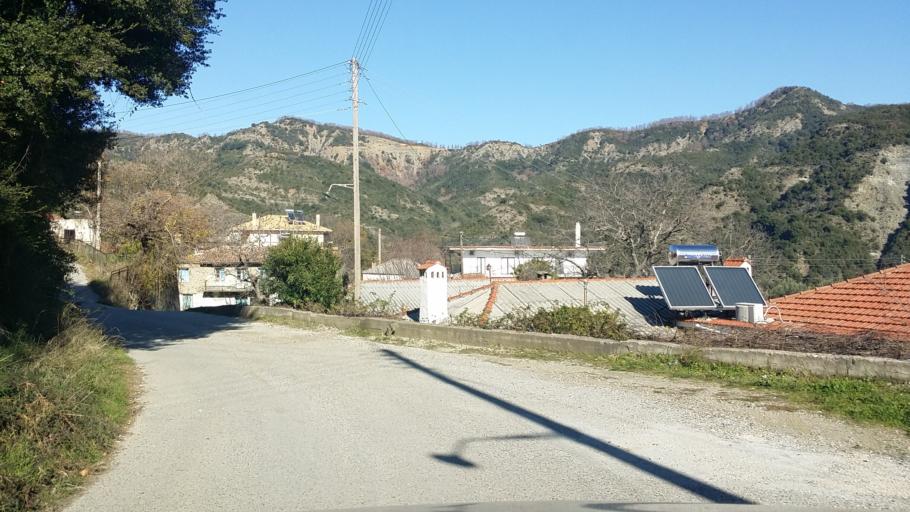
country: GR
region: West Greece
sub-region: Nomos Aitolias kai Akarnanias
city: Krikellos
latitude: 39.0020
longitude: 21.2427
